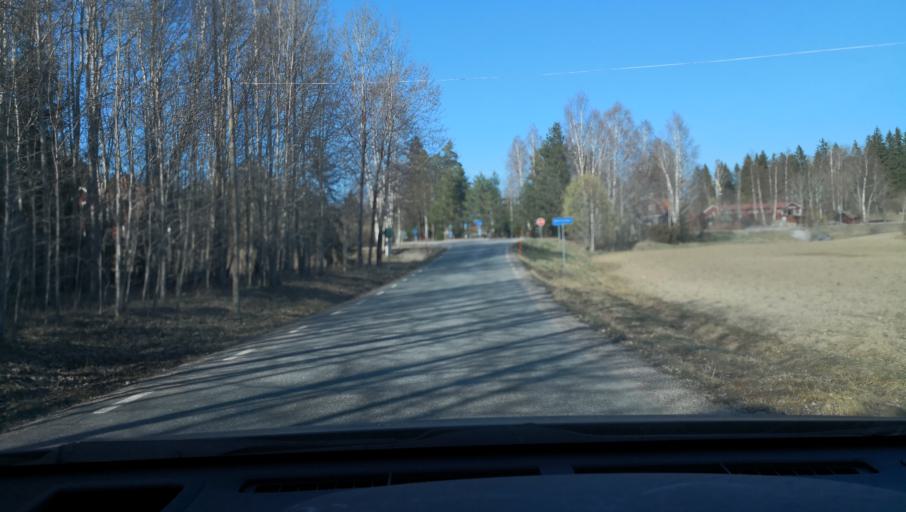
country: SE
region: Vaestmanland
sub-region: Sala Kommun
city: Sala
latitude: 59.9835
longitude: 16.4756
